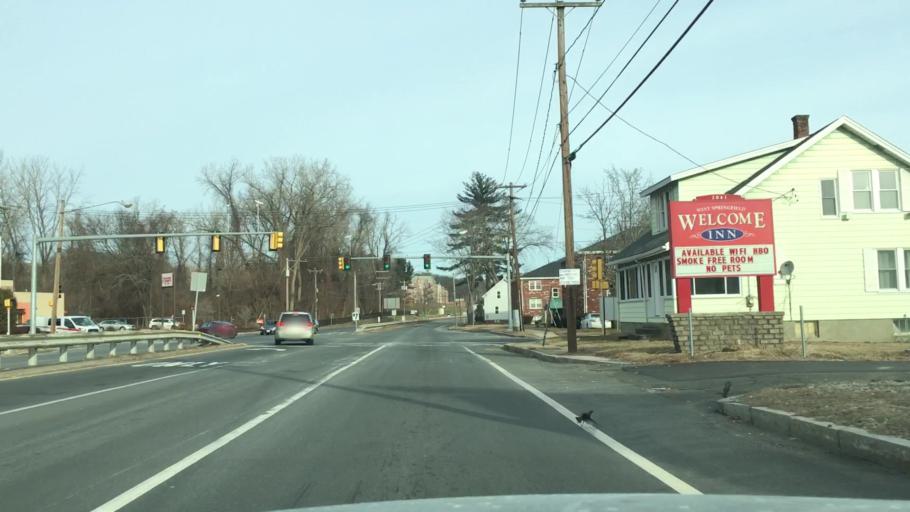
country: US
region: Massachusetts
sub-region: Hampden County
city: Chicopee
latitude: 42.1586
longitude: -72.6330
